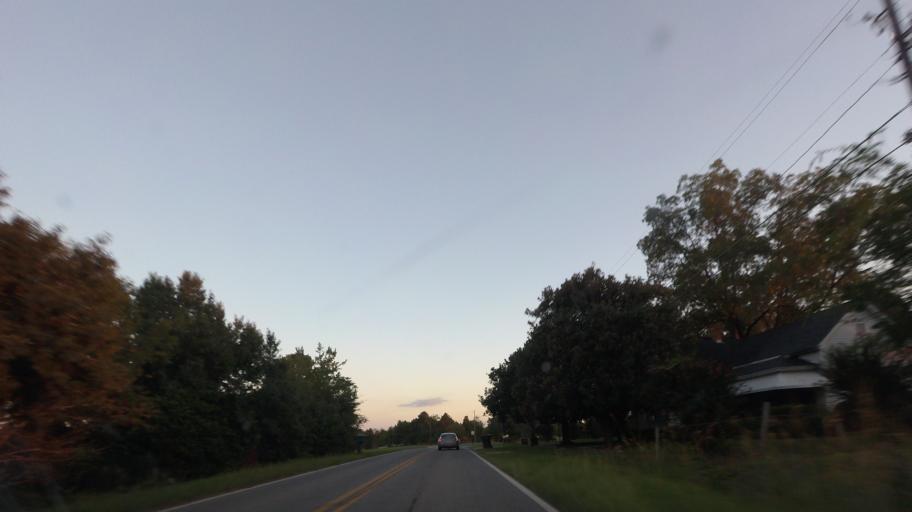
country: US
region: Georgia
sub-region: Peach County
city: Byron
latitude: 32.7295
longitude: -83.7215
